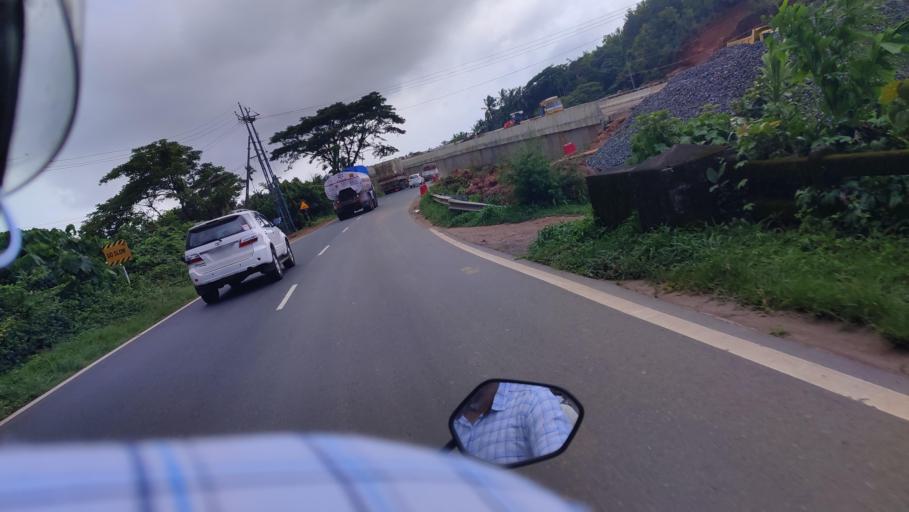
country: IN
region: Kerala
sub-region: Kasaragod District
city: Nileshwar
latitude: 12.2409
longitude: 75.1489
